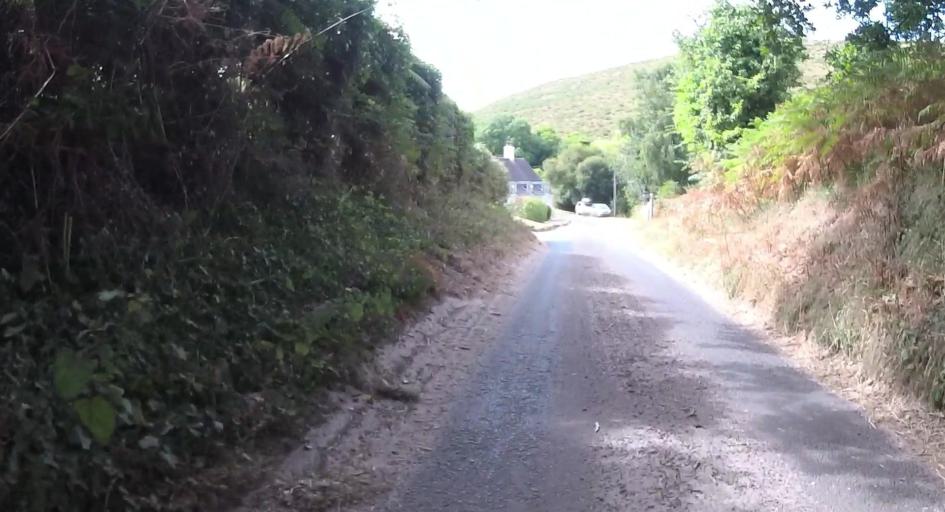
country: GB
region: England
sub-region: Dorset
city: Wareham
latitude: 50.6383
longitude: -2.0512
